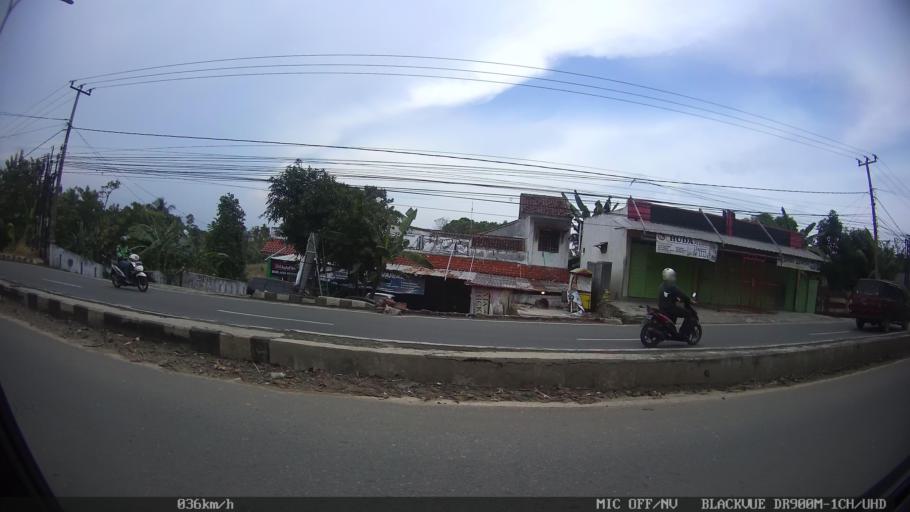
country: ID
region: Lampung
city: Kedaton
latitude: -5.3807
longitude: 105.2221
